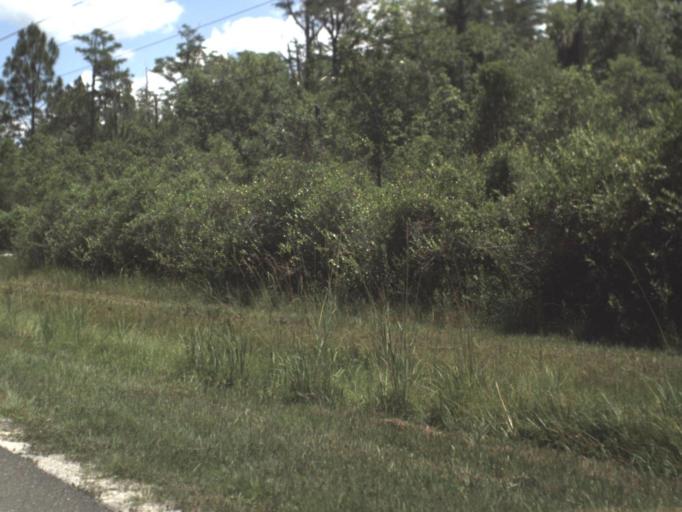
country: US
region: Florida
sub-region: Clay County
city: Keystone Heights
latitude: 29.7429
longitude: -82.0519
